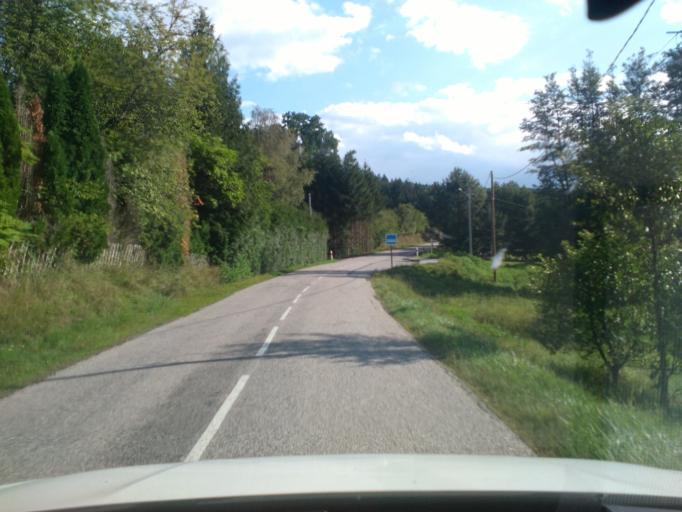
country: FR
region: Lorraine
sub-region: Departement des Vosges
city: Taintrux
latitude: 48.2312
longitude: 6.9046
